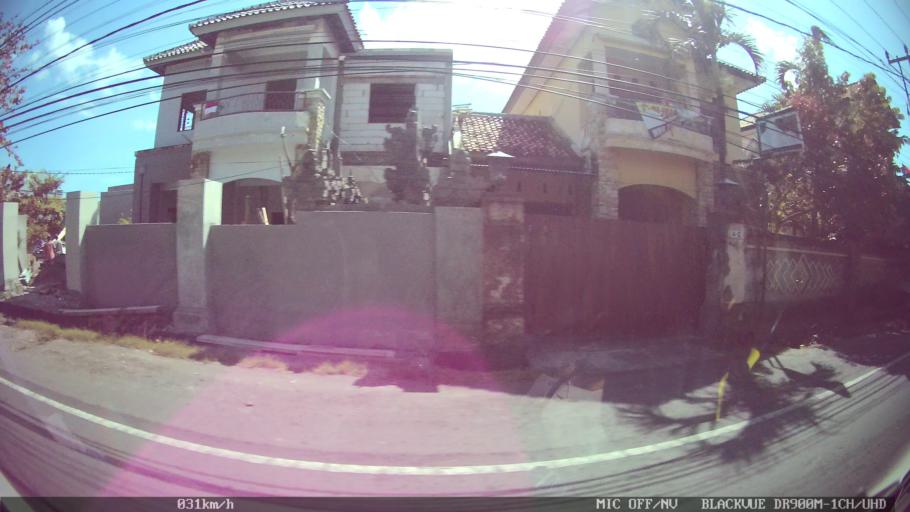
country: ID
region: Bali
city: Banjar Kertasari
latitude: -8.6393
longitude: 115.1748
